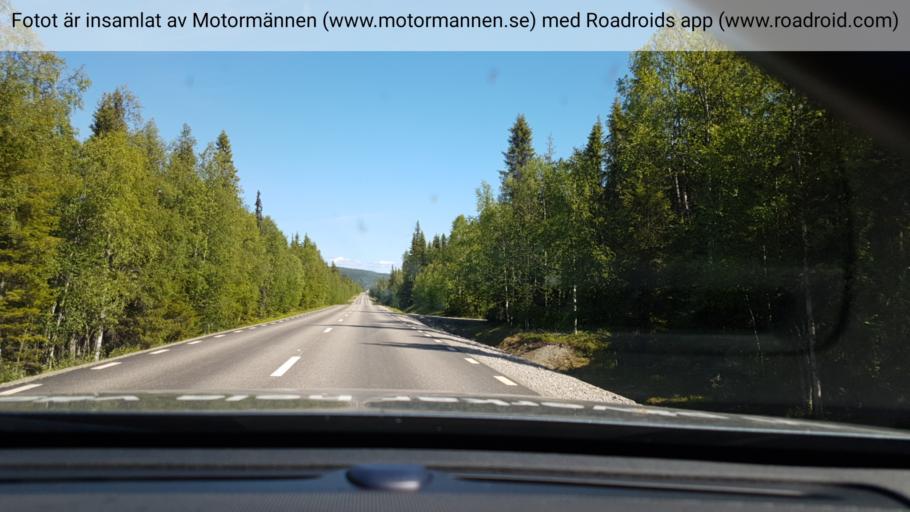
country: SE
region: Vaesterbotten
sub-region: Asele Kommun
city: Insjon
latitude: 64.7257
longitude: 17.5866
